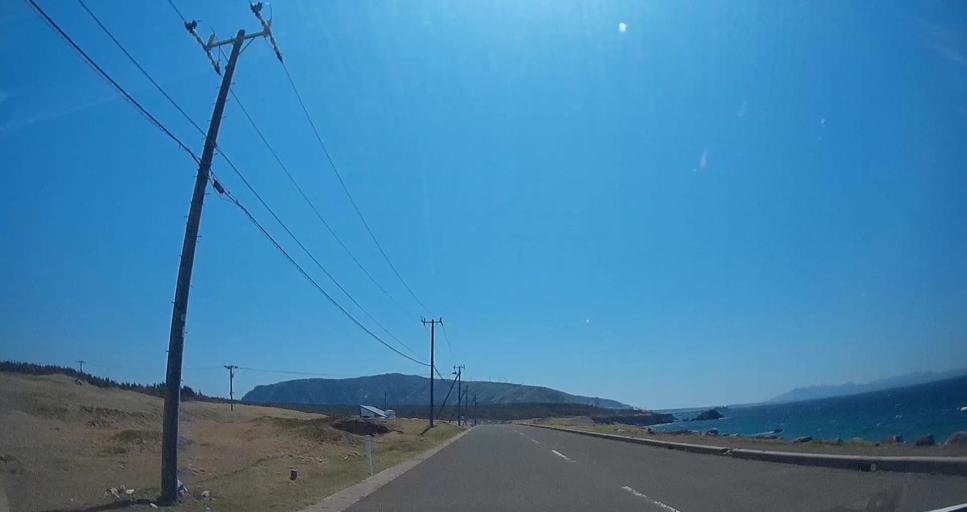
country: JP
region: Aomori
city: Mutsu
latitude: 41.4287
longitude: 141.4604
